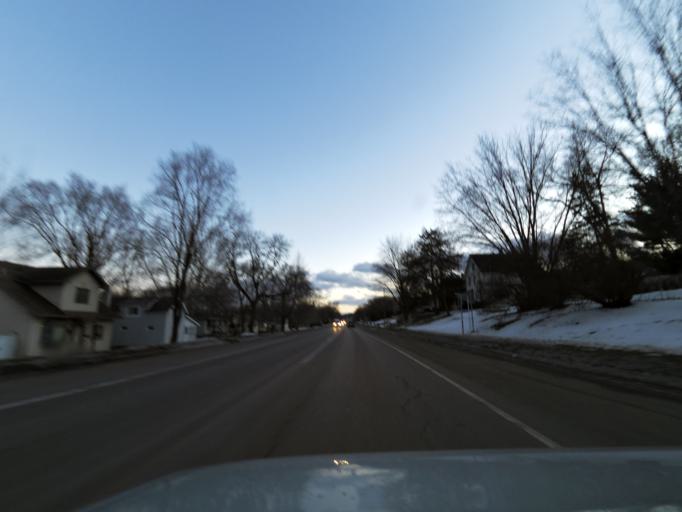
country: US
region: Minnesota
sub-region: Washington County
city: Bayport
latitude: 45.0140
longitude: -92.7796
